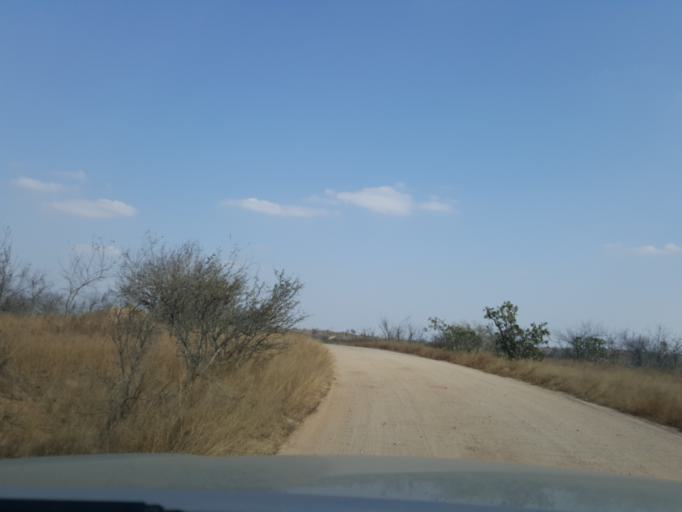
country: ZA
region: Mpumalanga
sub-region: Ehlanzeni District
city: Komatipoort
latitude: -25.2942
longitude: 31.7605
